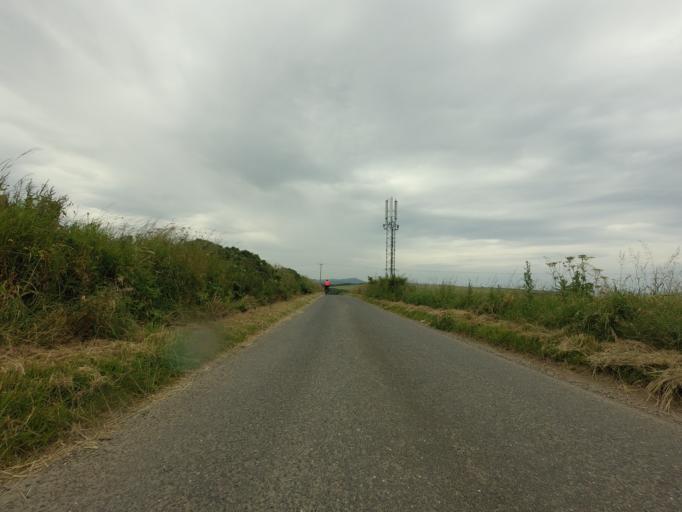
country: GB
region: Scotland
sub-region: Aberdeenshire
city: Portsoy
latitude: 57.6793
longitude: -2.6765
